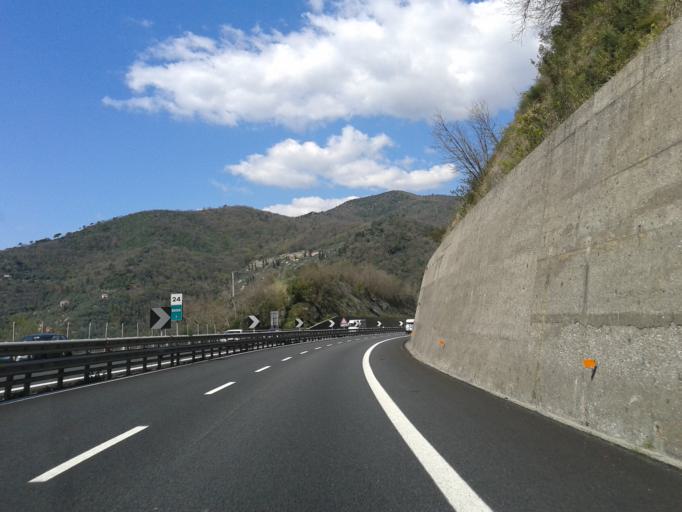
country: IT
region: Liguria
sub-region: Provincia di Genova
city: Avegno
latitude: 44.3695
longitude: 9.1566
